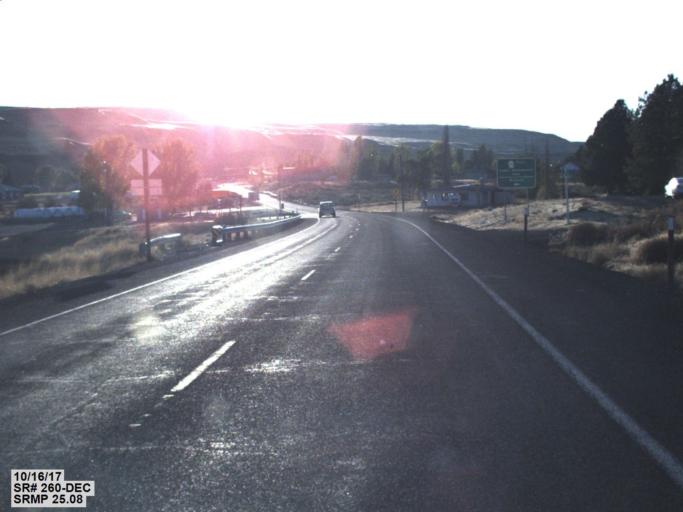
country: US
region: Washington
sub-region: Franklin County
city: Connell
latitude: 46.6451
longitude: -118.5511
